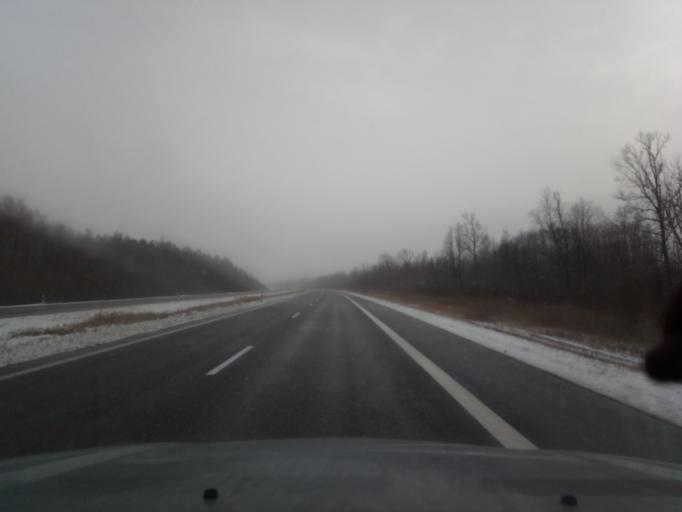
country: LT
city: Ramygala
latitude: 55.5749
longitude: 24.4693
